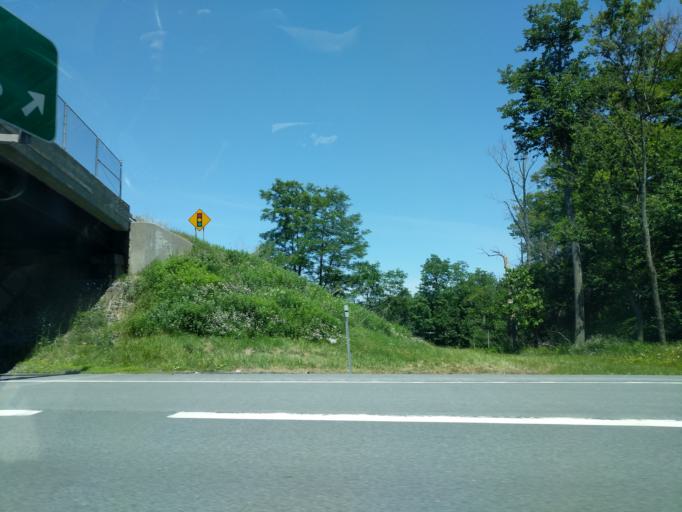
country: US
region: New York
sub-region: Sullivan County
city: Monticello
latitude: 41.6629
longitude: -74.6771
